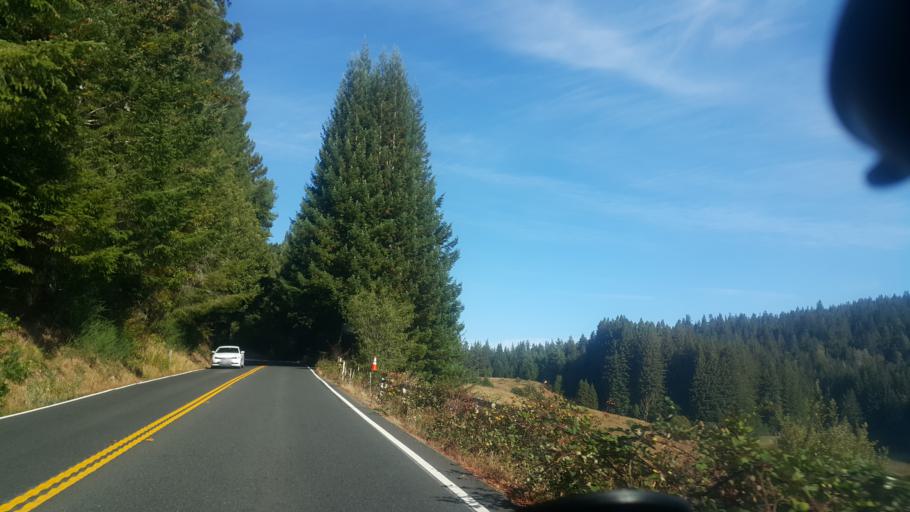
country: US
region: California
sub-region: Mendocino County
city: Fort Bragg
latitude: 39.3553
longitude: -123.6151
